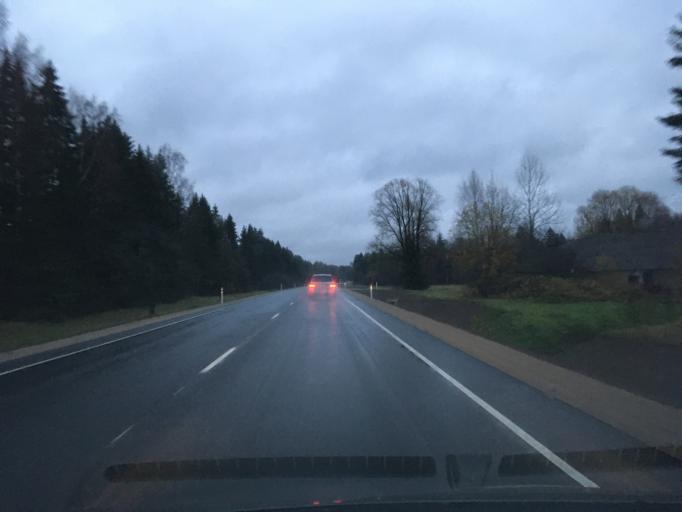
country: EE
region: Laeaene
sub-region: Lihula vald
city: Lihula
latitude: 58.6567
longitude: 23.7212
